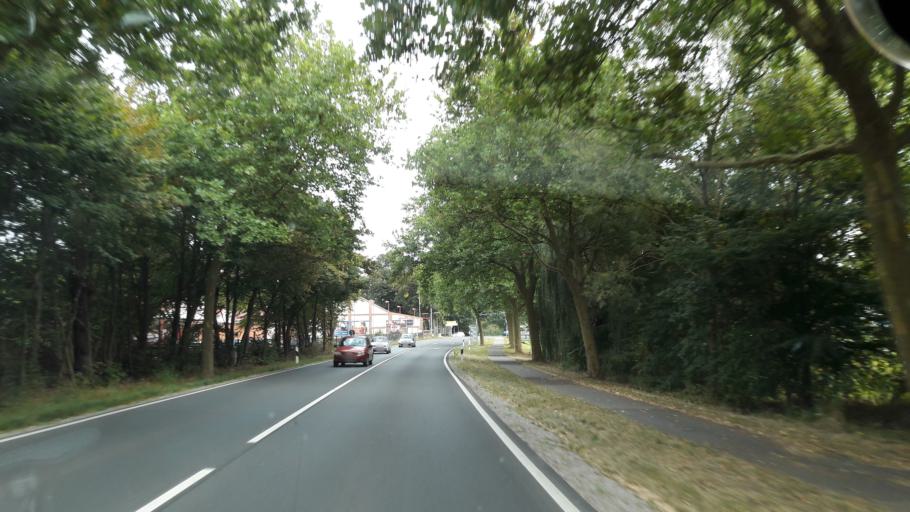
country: DE
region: Lower Saxony
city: Bockenem
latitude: 52.0103
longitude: 10.1224
